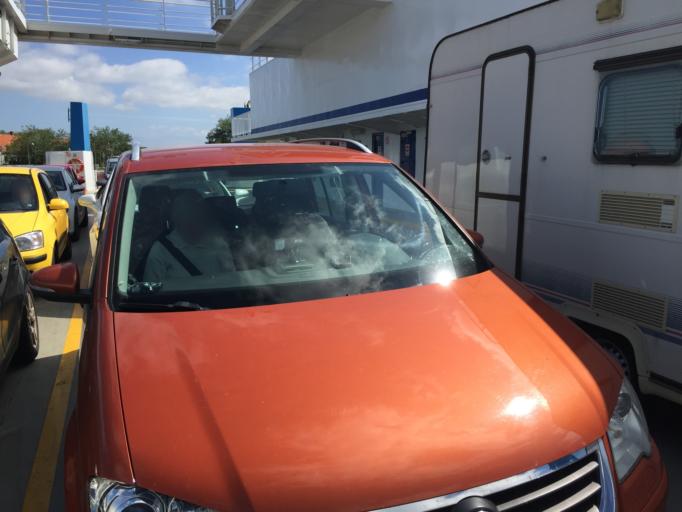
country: DK
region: South Denmark
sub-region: Sonderborg Kommune
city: Nordborg
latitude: 55.0074
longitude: 9.6913
